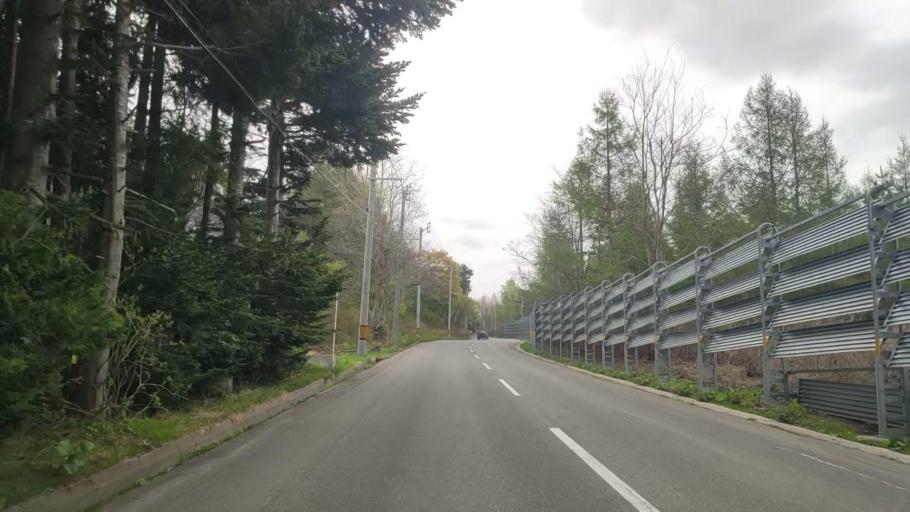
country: JP
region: Aomori
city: Aomori Shi
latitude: 40.7511
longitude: 140.8165
